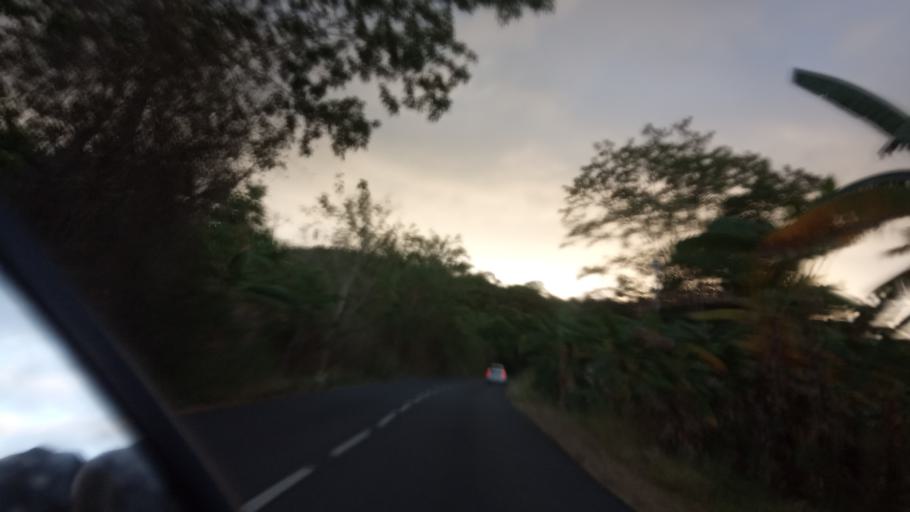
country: YT
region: Chirongui
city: Chirongui
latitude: -12.9302
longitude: 45.1219
